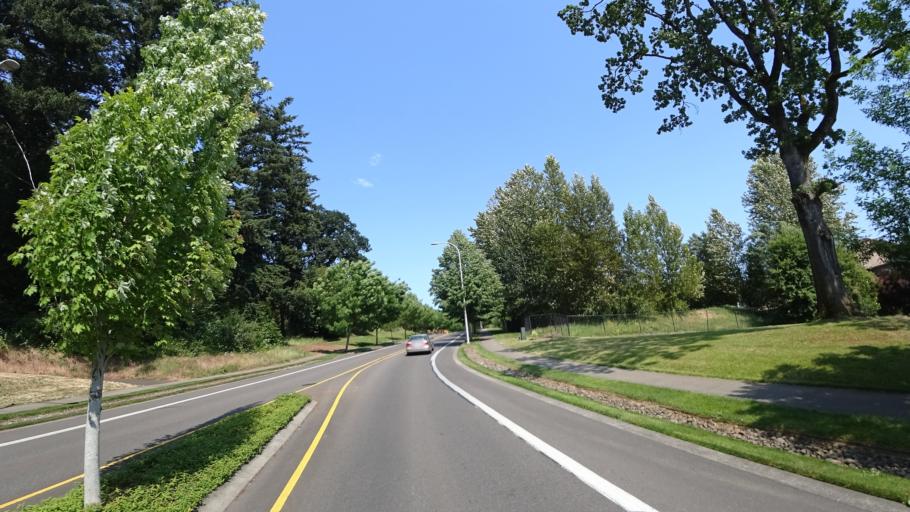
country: US
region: Oregon
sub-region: Clackamas County
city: Happy Valley
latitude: 45.4401
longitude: -122.5540
